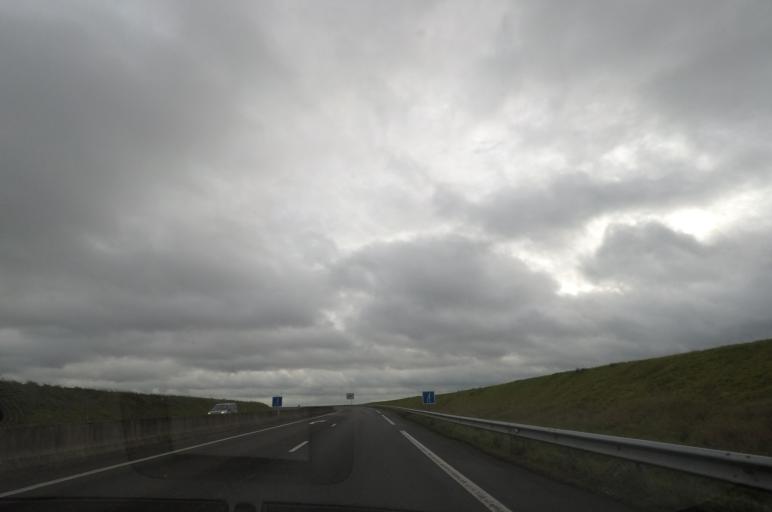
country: FR
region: Centre
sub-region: Departement du Loir-et-Cher
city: Saint-Sulpice-de-Pommeray
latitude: 47.6667
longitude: 1.2416
